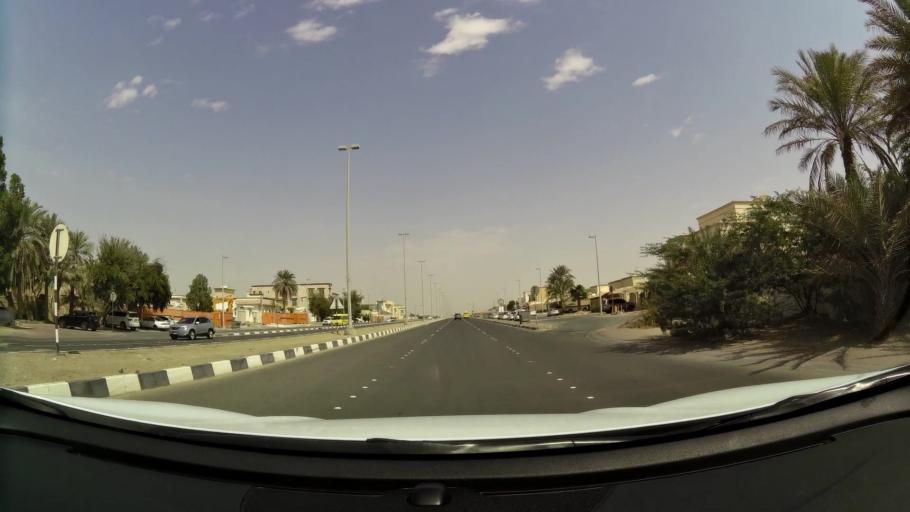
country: AE
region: Abu Dhabi
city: Abu Dhabi
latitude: 24.2949
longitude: 54.6437
